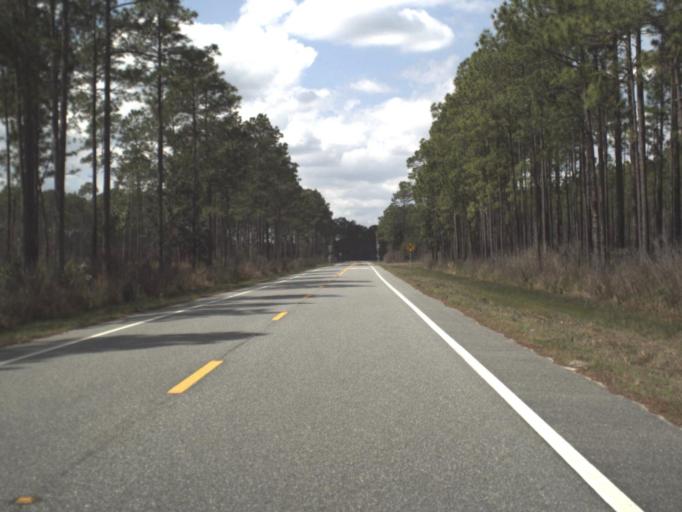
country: US
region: Florida
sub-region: Franklin County
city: Apalachicola
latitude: 29.8454
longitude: -84.9642
